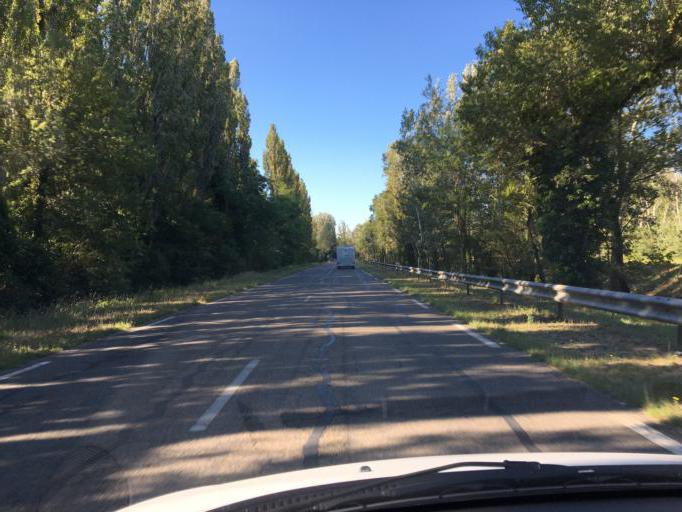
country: FR
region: Provence-Alpes-Cote d'Azur
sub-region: Departement du Vaucluse
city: Avignon
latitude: 43.9682
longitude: 4.8188
